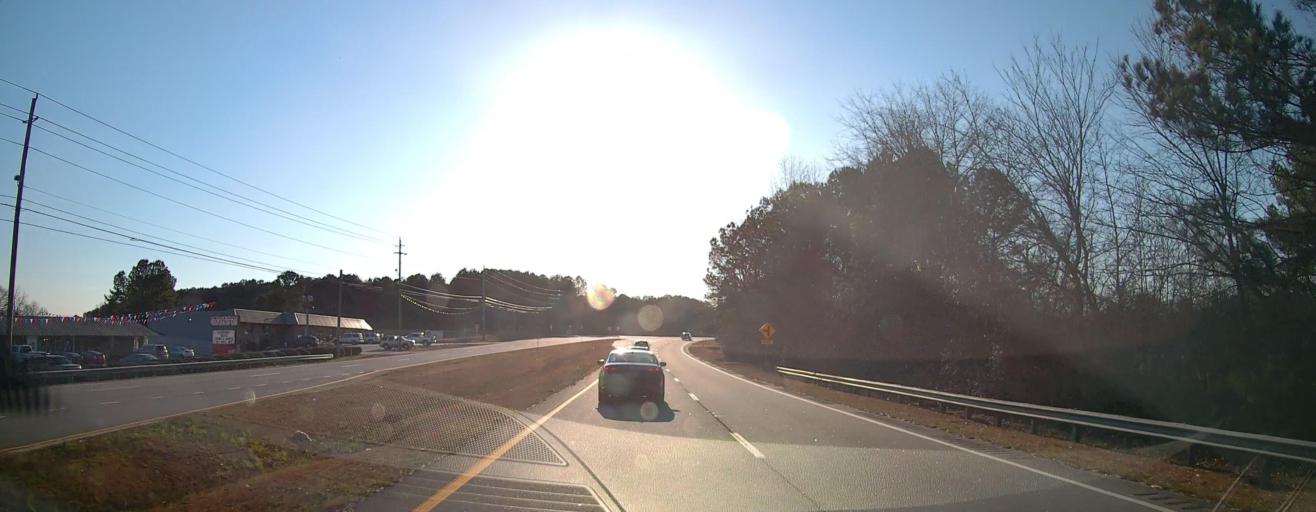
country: US
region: Georgia
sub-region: Fayette County
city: Shannon
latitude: 33.4438
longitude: -84.5294
